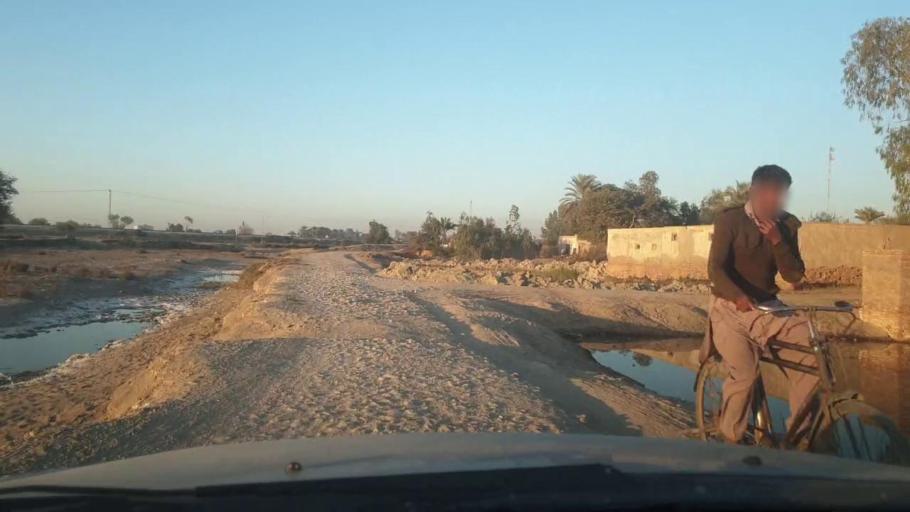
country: PK
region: Sindh
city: Pano Aqil
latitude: 27.9160
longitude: 69.1939
